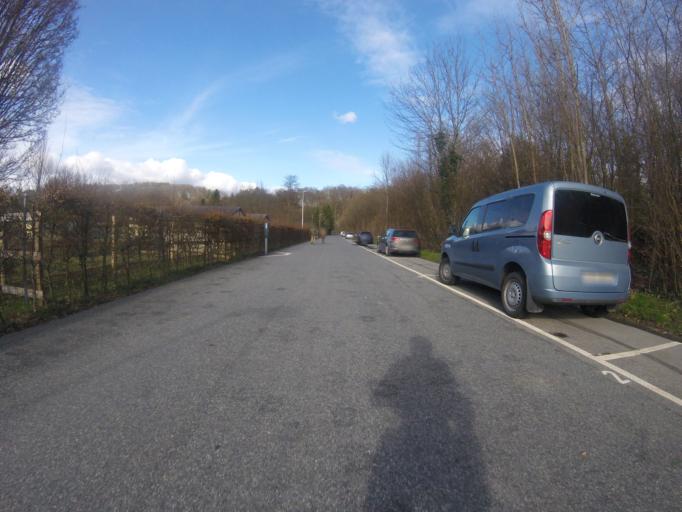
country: CH
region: Bern
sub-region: Bern-Mittelland District
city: Wohlen
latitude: 46.9637
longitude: 7.3845
